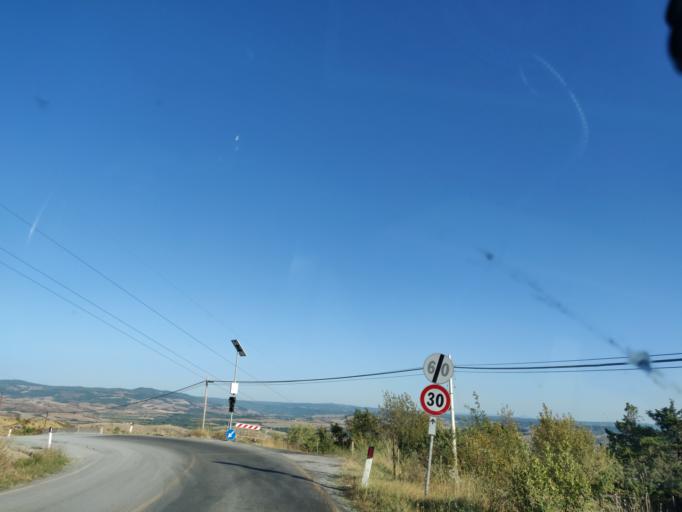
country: IT
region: Tuscany
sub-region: Provincia di Siena
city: Piancastagnaio
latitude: 42.8401
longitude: 11.7027
